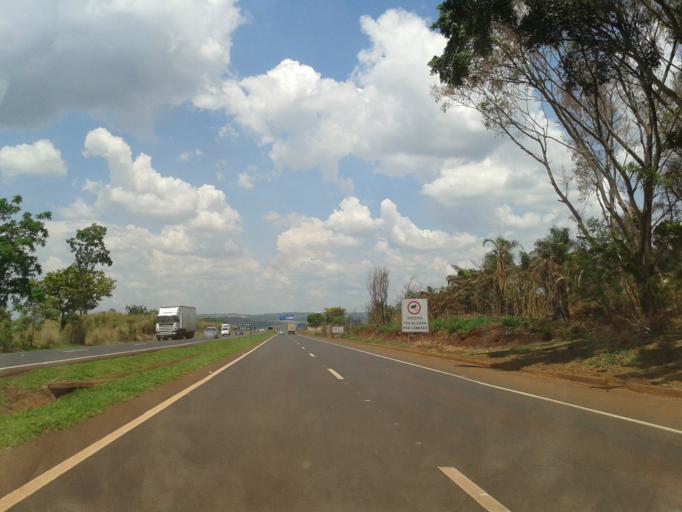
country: BR
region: Minas Gerais
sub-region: Araguari
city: Araguari
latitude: -18.7397
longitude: -48.2291
